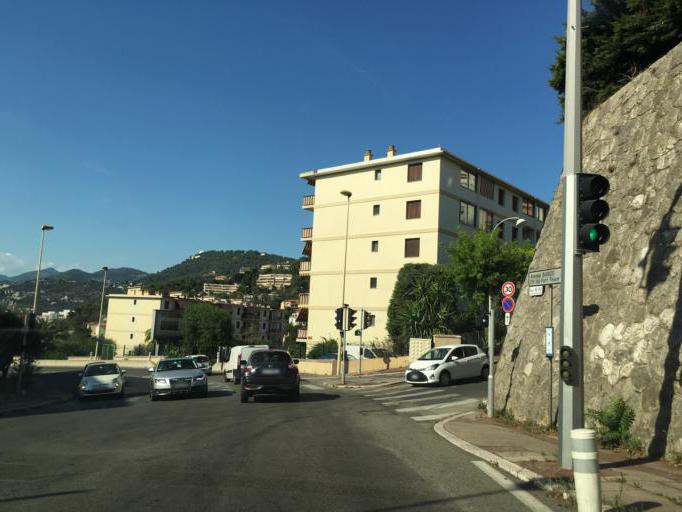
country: FR
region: Provence-Alpes-Cote d'Azur
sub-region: Departement des Alpes-Maritimes
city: Villefranche-sur-Mer
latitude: 43.7017
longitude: 7.2946
